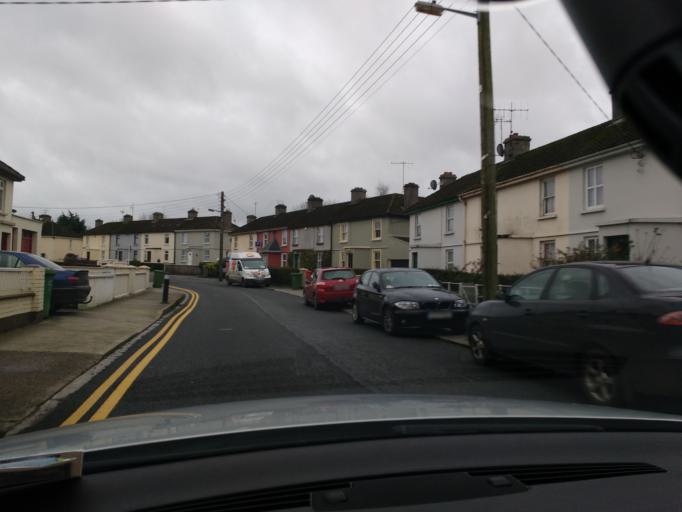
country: IE
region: Munster
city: Thurles
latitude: 52.6760
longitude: -7.8191
